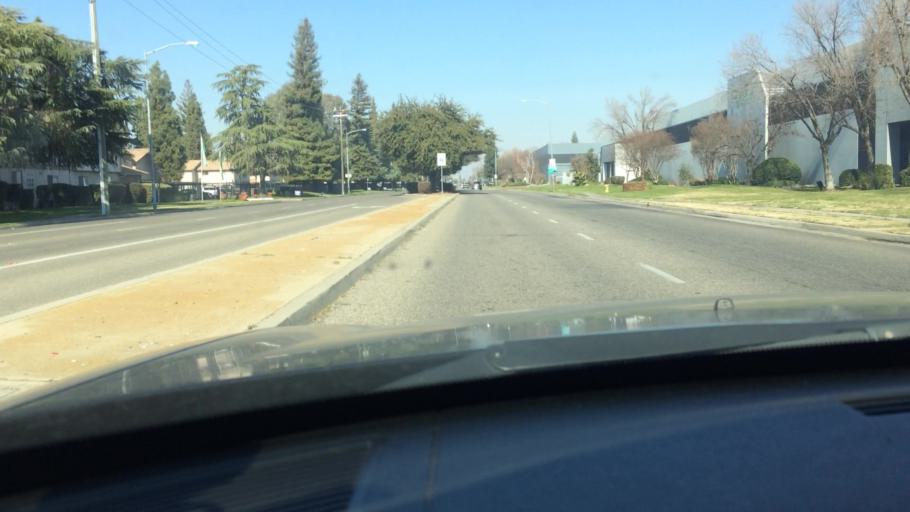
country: US
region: California
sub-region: Fresno County
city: Tarpey Village
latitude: 36.7869
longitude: -119.7181
